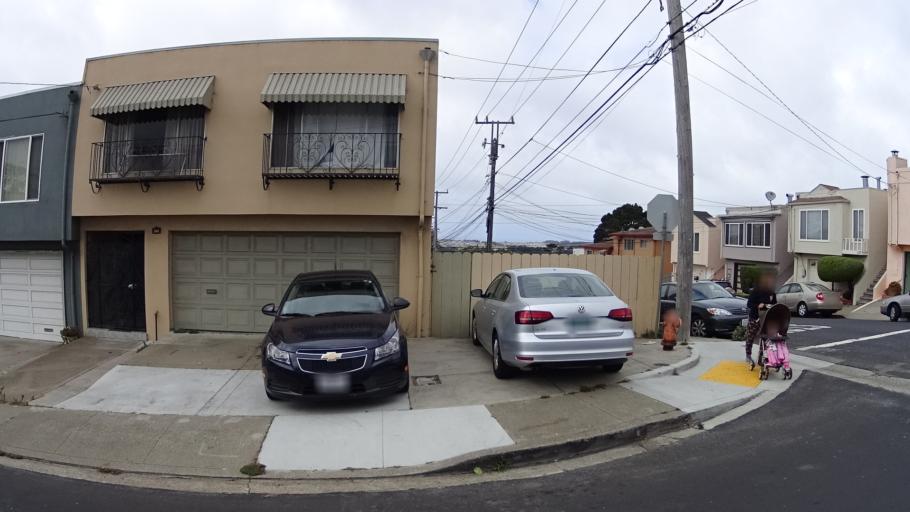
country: US
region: California
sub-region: San Mateo County
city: Daly City
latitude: 37.6959
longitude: -122.4610
